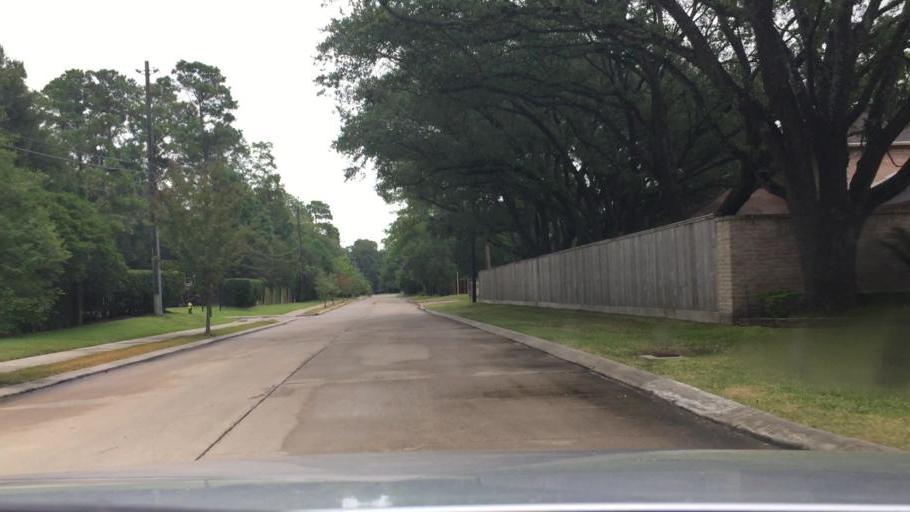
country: US
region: Texas
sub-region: Harris County
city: Piney Point Village
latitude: 29.7663
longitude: -95.5124
